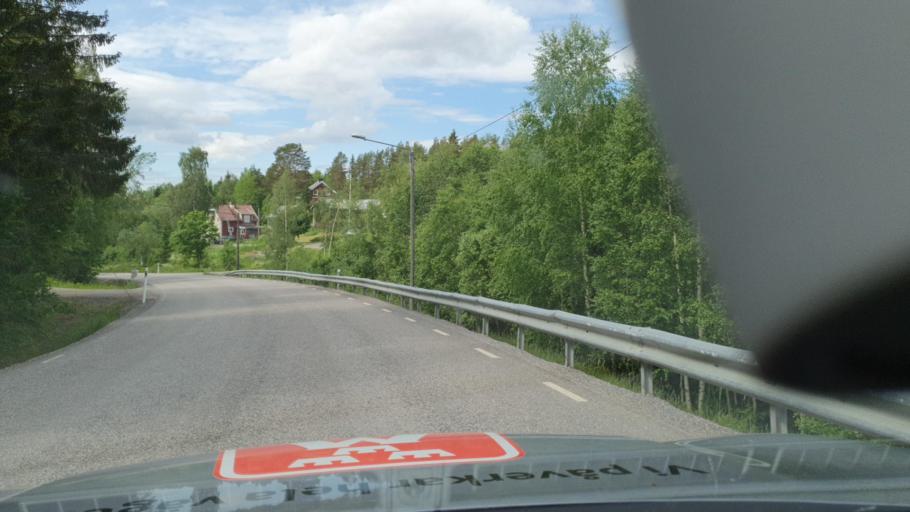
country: SE
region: Vaesternorrland
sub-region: Kramfors Kommun
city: Kramfors
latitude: 62.9221
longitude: 17.9370
